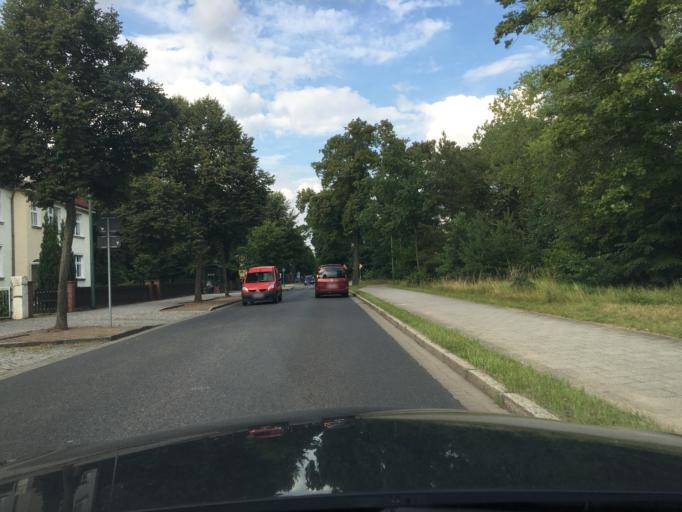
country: DE
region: Mecklenburg-Vorpommern
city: Neustrelitz
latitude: 53.3693
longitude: 13.0707
